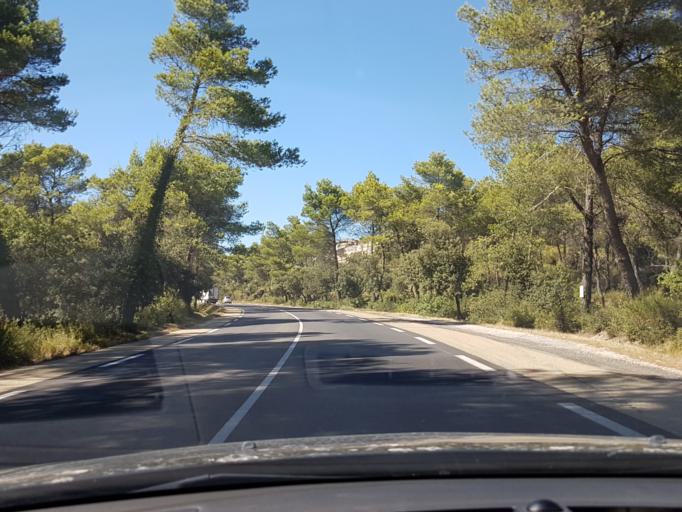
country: FR
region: Provence-Alpes-Cote d'Azur
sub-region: Departement des Bouches-du-Rhone
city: Orgon
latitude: 43.8086
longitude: 5.0253
